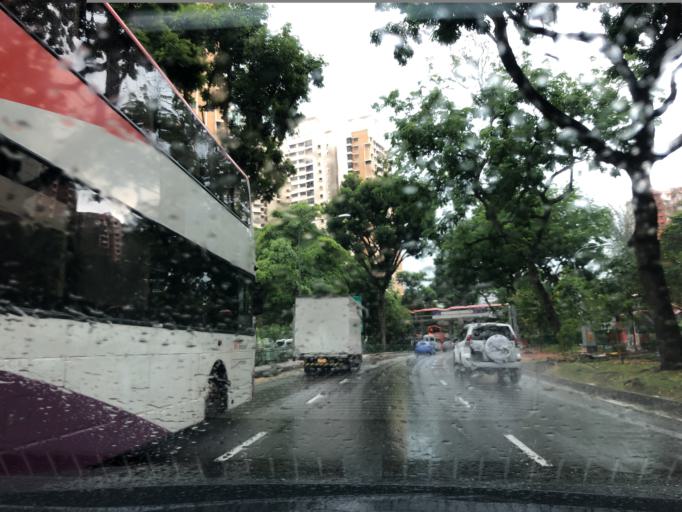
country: SG
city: Singapore
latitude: 1.2849
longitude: 103.8253
